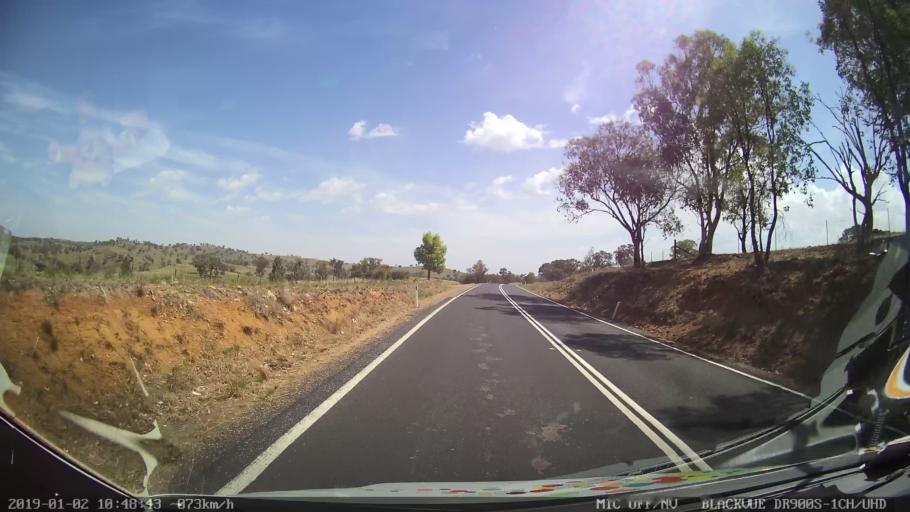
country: AU
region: New South Wales
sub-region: Cootamundra
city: Cootamundra
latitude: -34.7335
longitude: 148.2777
